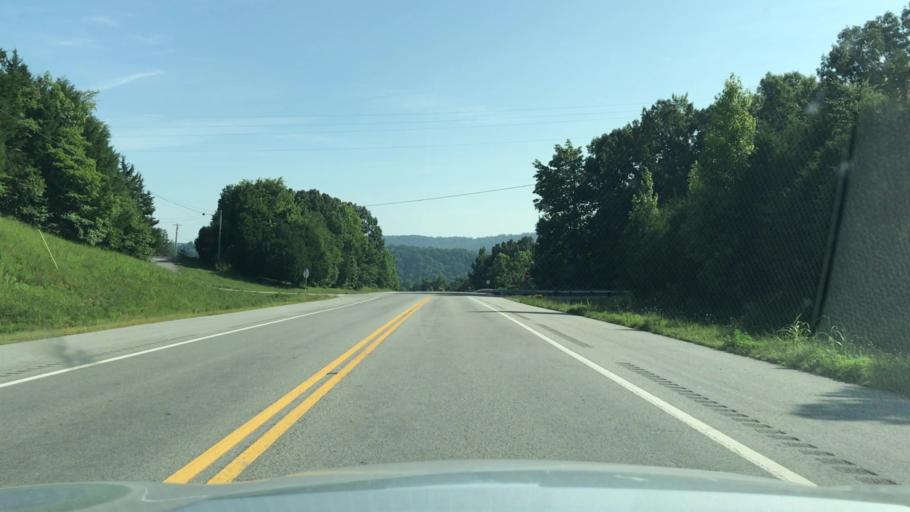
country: US
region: Tennessee
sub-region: Pickett County
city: Byrdstown
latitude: 36.5219
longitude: -85.1665
